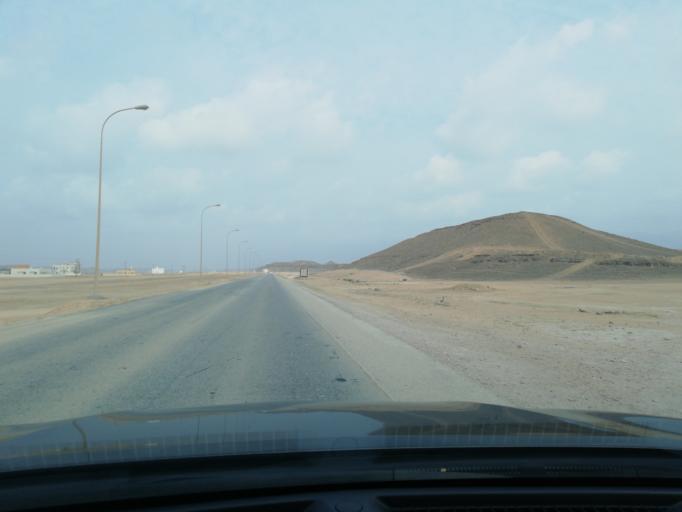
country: OM
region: Zufar
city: Salalah
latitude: 16.9495
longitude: 53.9378
